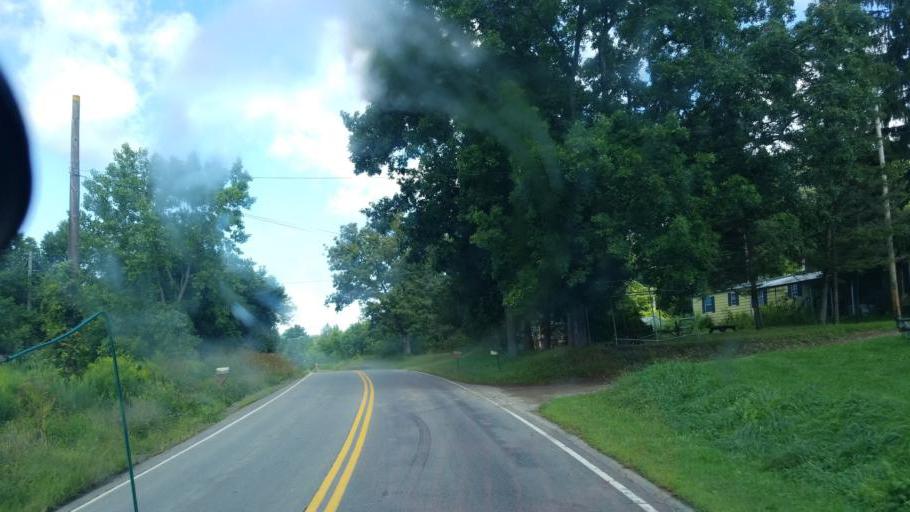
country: US
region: New York
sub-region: Steuben County
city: Canisteo
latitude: 42.3006
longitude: -77.6309
